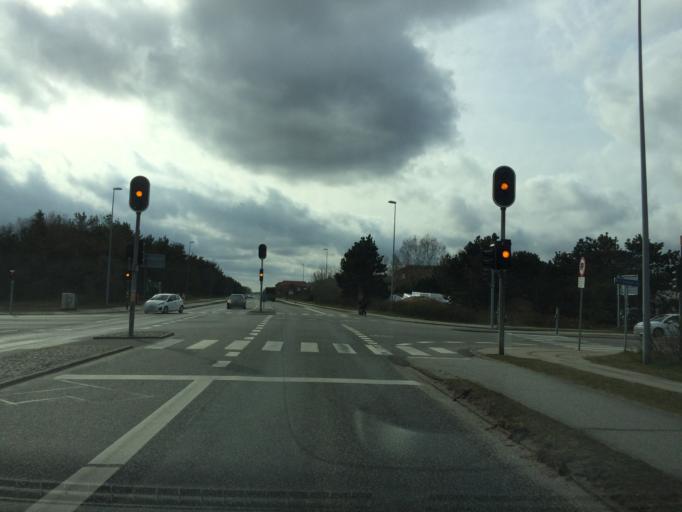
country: DK
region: Central Jutland
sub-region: Norddjurs Kommune
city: Grenaa
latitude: 56.4069
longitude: 10.8878
